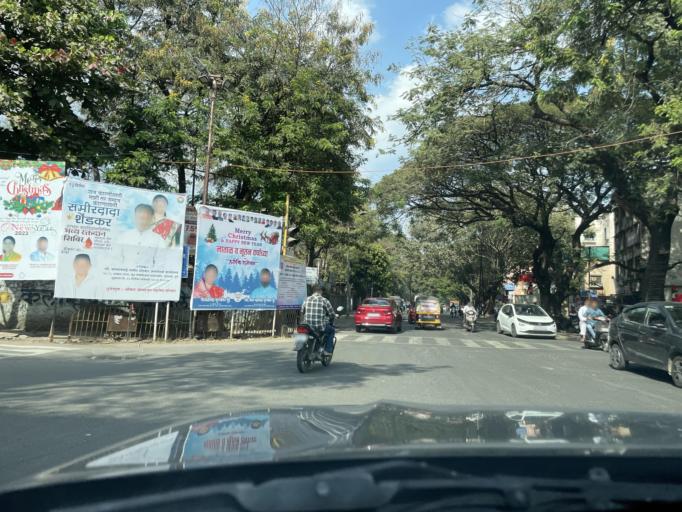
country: IN
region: Maharashtra
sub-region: Pune Division
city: Pune
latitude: 18.4950
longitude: 73.9000
